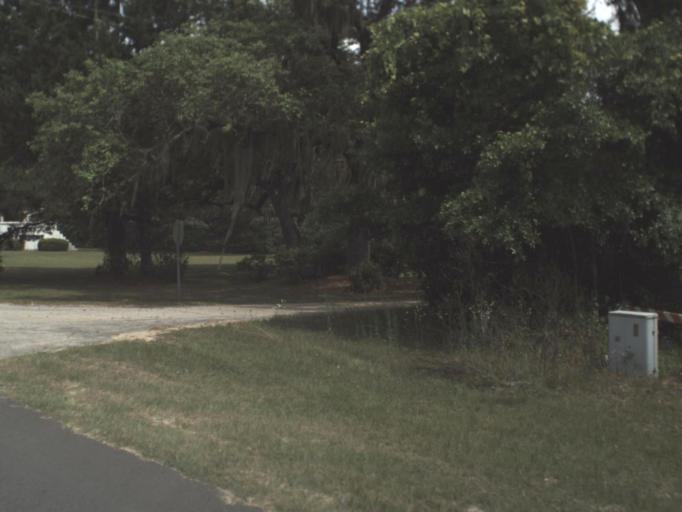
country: US
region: Florida
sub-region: Putnam County
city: Interlachen
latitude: 29.6259
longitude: -81.8977
